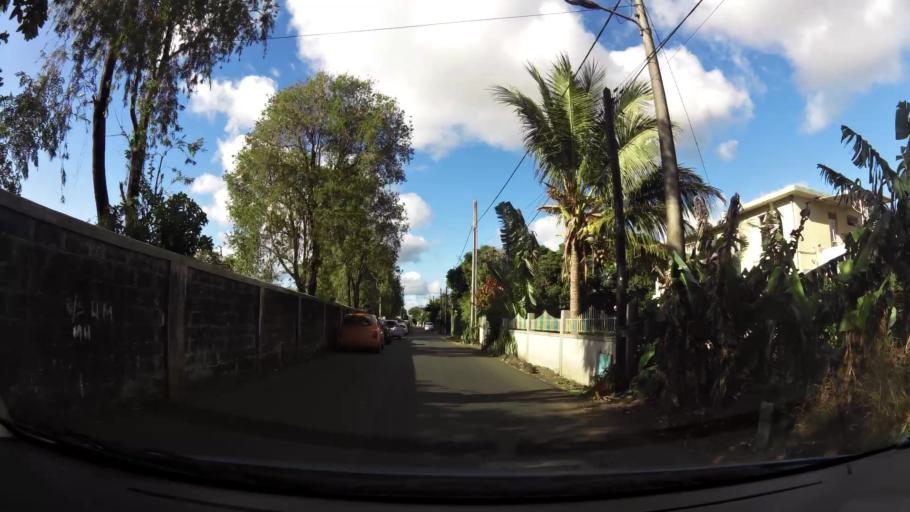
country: MU
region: Plaines Wilhems
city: Vacoas
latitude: -20.2902
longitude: 57.4907
